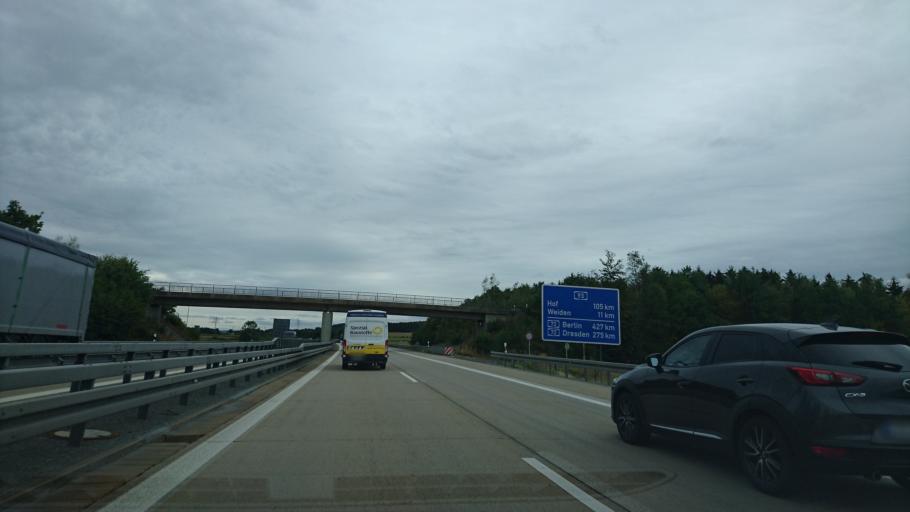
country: DE
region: Bavaria
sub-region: Upper Palatinate
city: Luhe-Wildenau
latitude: 49.5989
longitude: 12.1473
